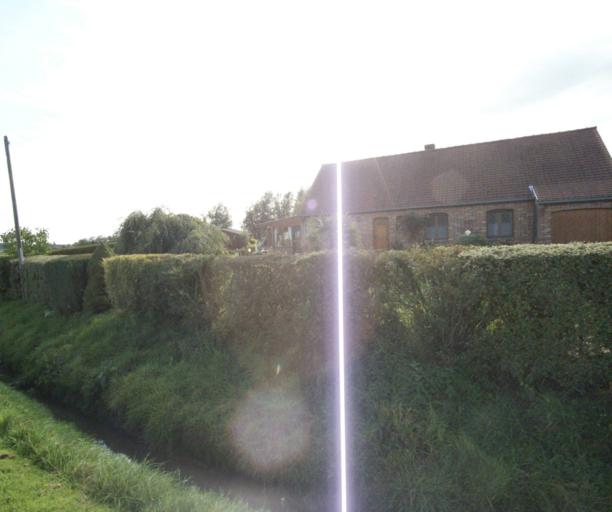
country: FR
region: Nord-Pas-de-Calais
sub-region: Departement du Nord
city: Radinghem-en-Weppes
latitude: 50.6317
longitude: 2.9157
